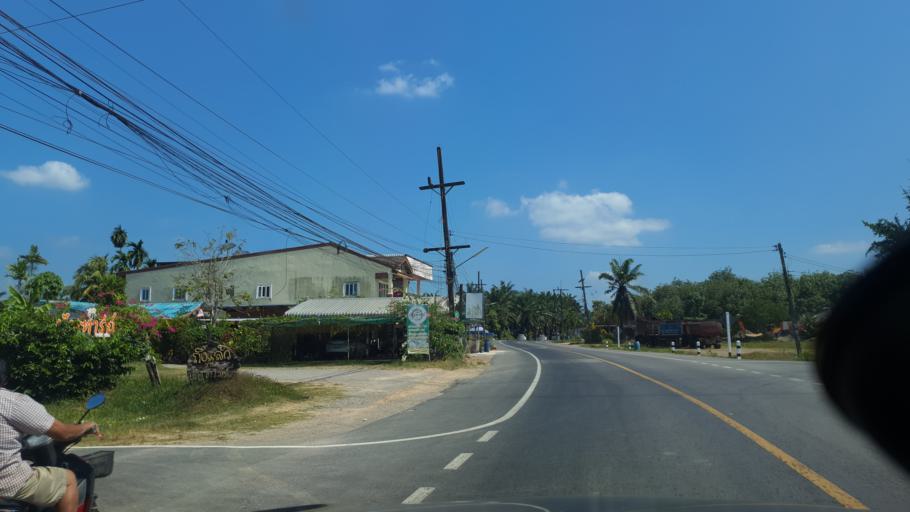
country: TH
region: Krabi
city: Khlong Thom
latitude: 7.9387
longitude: 99.1479
